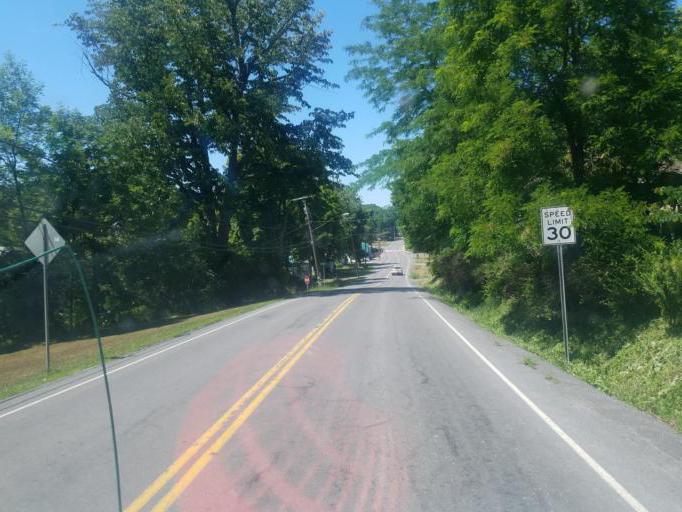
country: US
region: New York
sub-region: Yates County
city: Penn Yan
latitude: 42.7557
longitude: -77.0136
